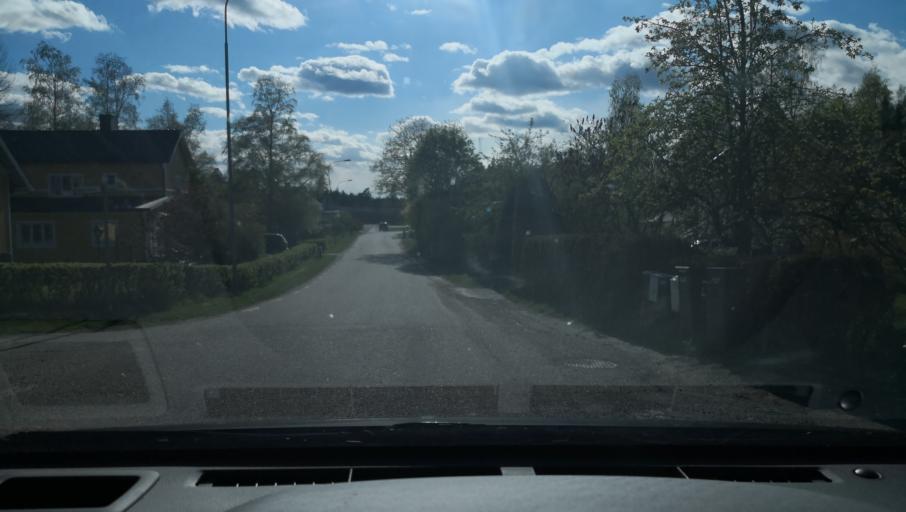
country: SE
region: OErebro
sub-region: Askersunds Kommun
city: Asbro
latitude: 58.9489
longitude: 15.0453
